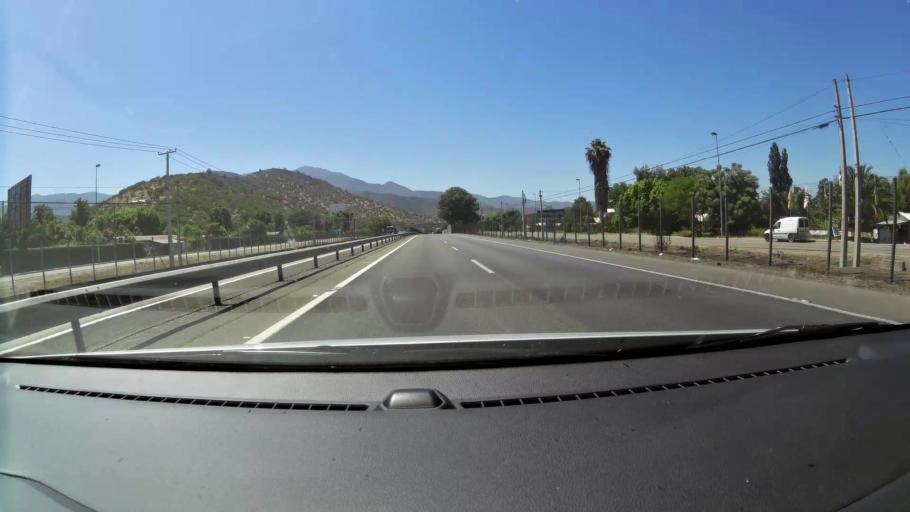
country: CL
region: Santiago Metropolitan
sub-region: Provincia de Chacabuco
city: Lampa
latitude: -33.4094
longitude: -71.0656
